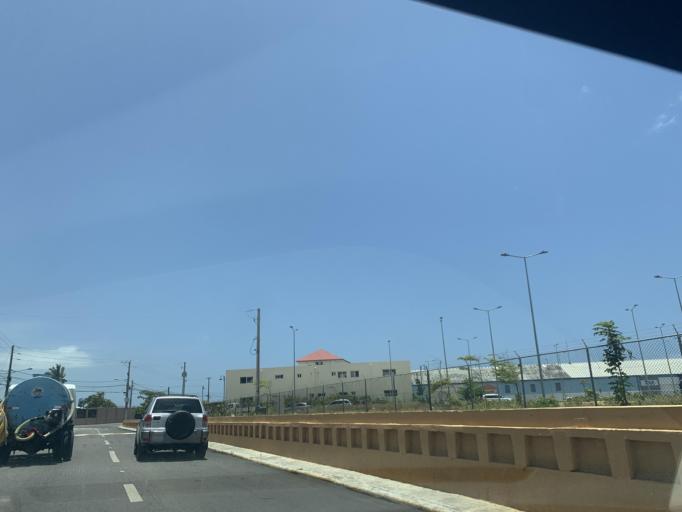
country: DO
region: Puerto Plata
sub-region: Puerto Plata
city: Puerto Plata
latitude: 19.7995
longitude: -70.6966
